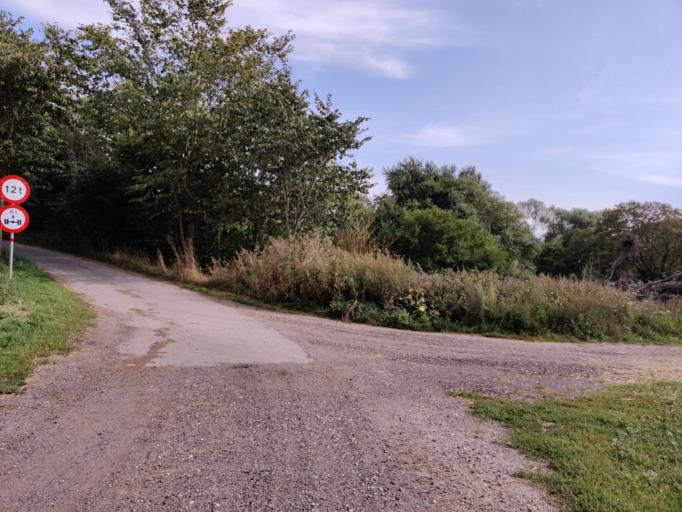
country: DK
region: Zealand
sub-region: Guldborgsund Kommune
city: Nykobing Falster
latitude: 54.7001
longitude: 11.9026
